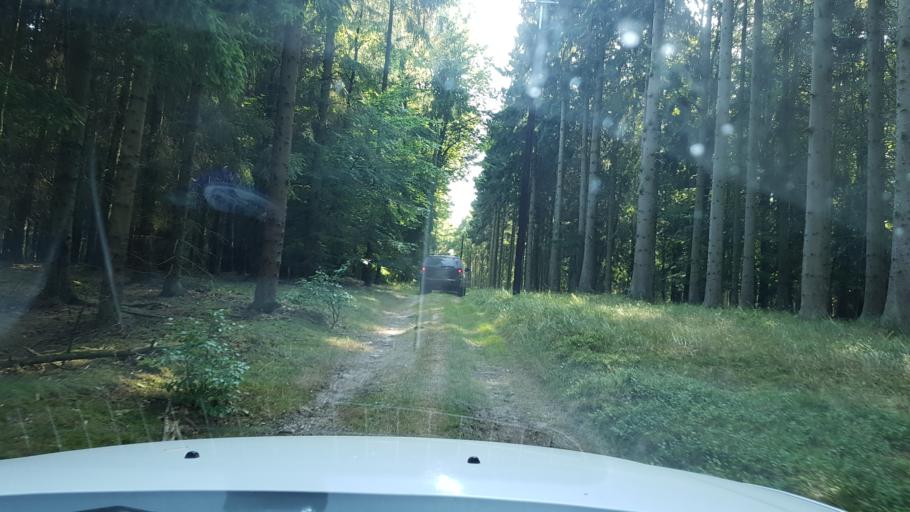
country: PL
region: West Pomeranian Voivodeship
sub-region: Powiat kamienski
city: Miedzyzdroje
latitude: 53.8782
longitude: 14.4935
